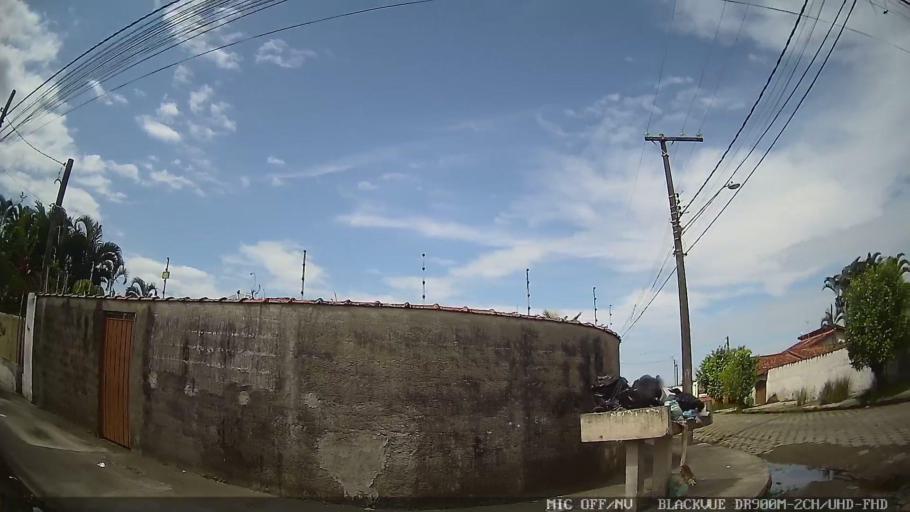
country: BR
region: Sao Paulo
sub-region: Itanhaem
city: Itanhaem
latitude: -24.2003
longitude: -46.8378
